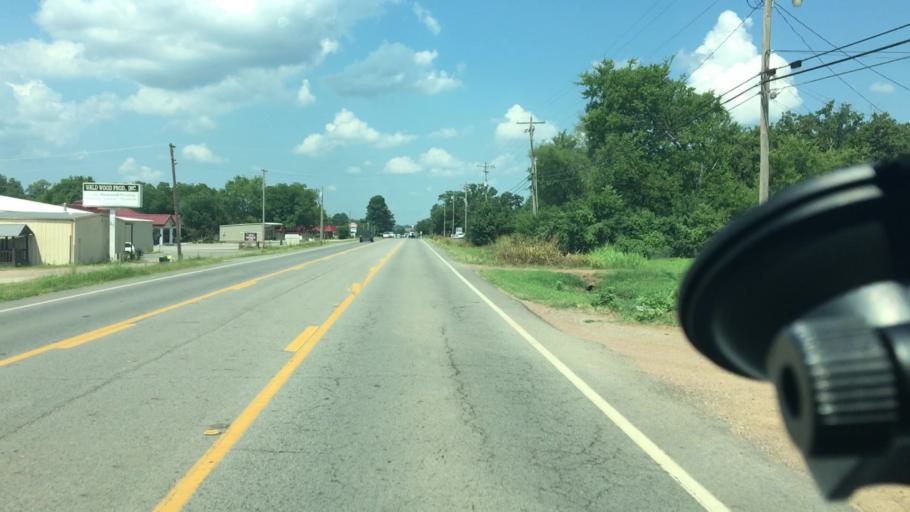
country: US
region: Arkansas
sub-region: Logan County
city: Paris
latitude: 35.2920
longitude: -93.7095
